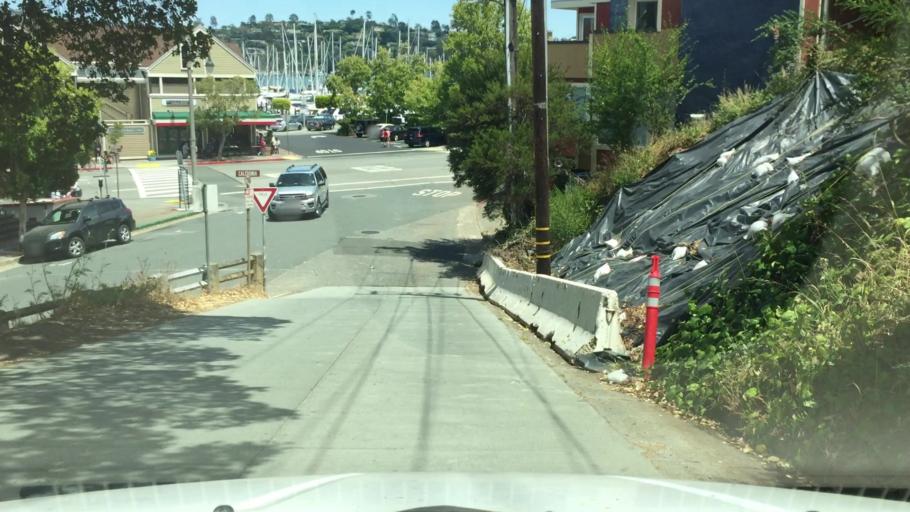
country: US
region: California
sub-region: Marin County
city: Sausalito
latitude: 37.8581
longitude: -122.4836
